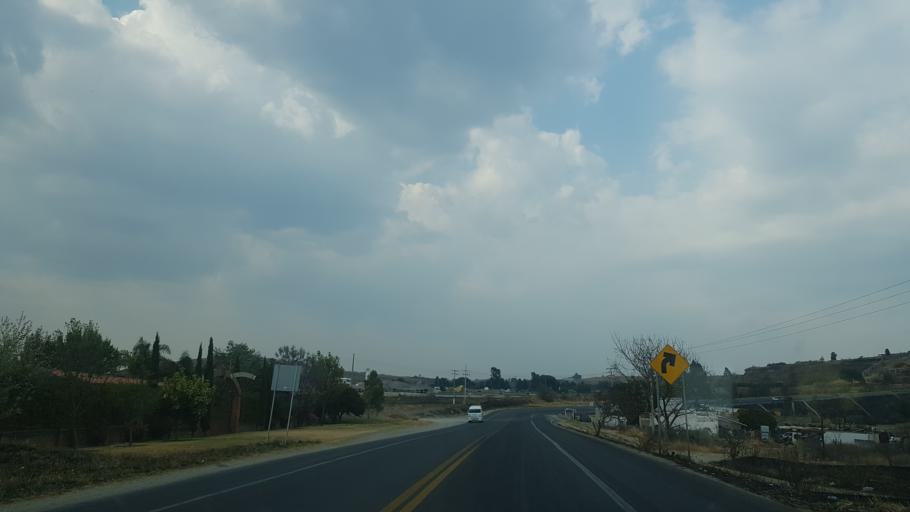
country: MX
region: Puebla
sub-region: Santa Isabel Cholula
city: San Martin Tlamapa
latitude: 18.9725
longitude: -98.3811
